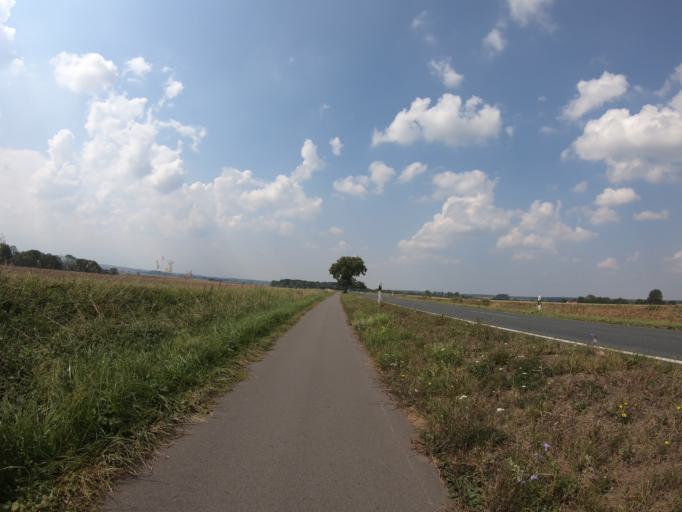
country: DE
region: Lower Saxony
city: Veltheim
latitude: 52.2052
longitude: 10.6770
